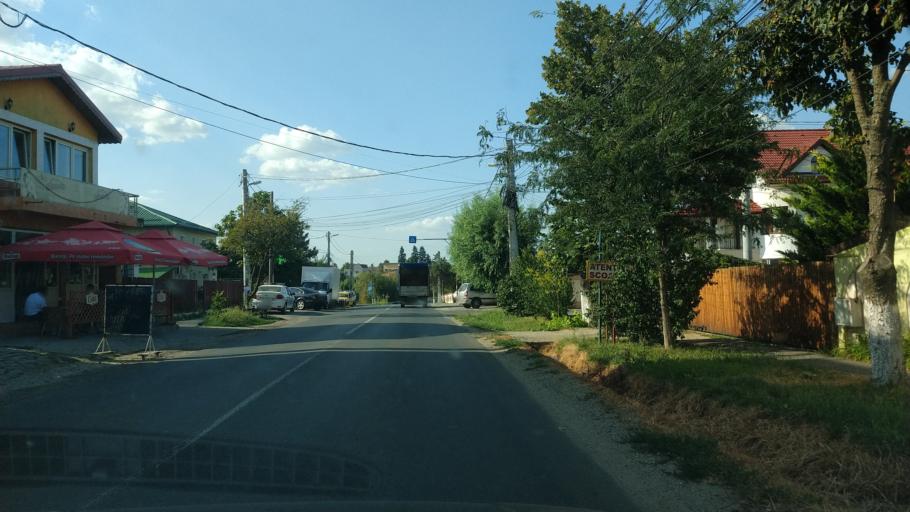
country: RO
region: Ilfov
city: Stefanestii de Jos
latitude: 44.5354
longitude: 26.2014
